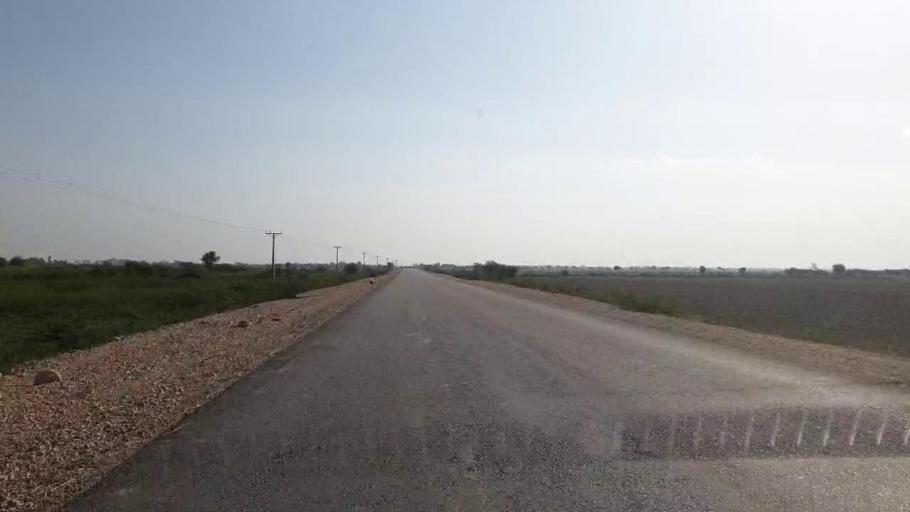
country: PK
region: Sindh
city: Tando Bago
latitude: 24.6574
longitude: 68.9954
